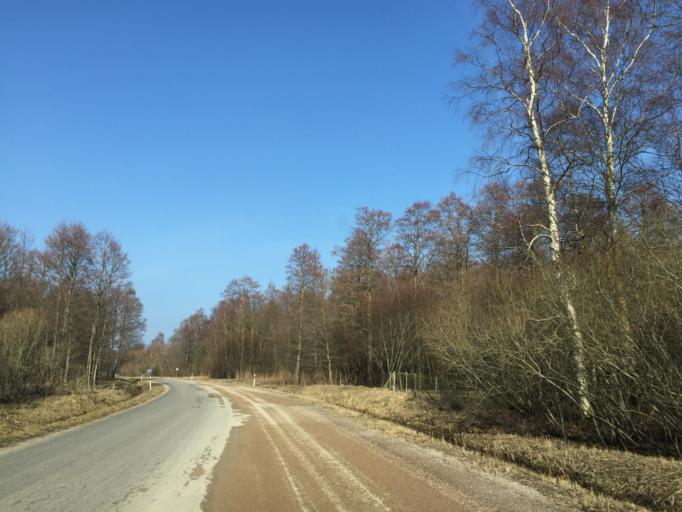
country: EE
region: Saare
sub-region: Kuressaare linn
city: Kuressaare
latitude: 58.0668
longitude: 22.1718
